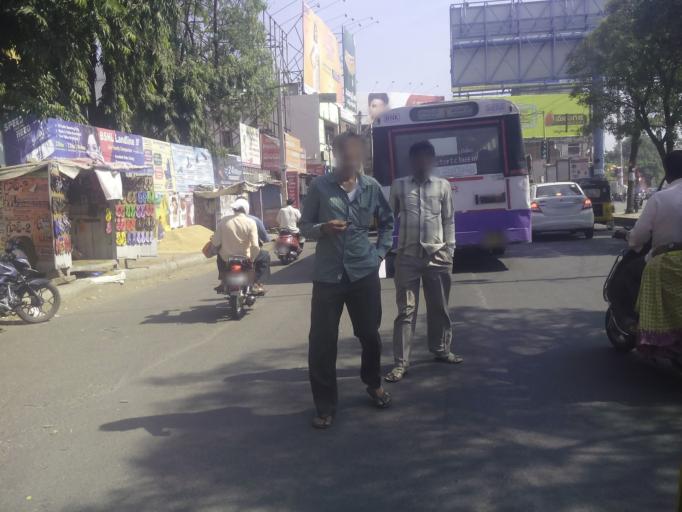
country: IN
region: Telangana
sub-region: Warangal
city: Warangal
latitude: 17.9884
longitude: 79.6010
